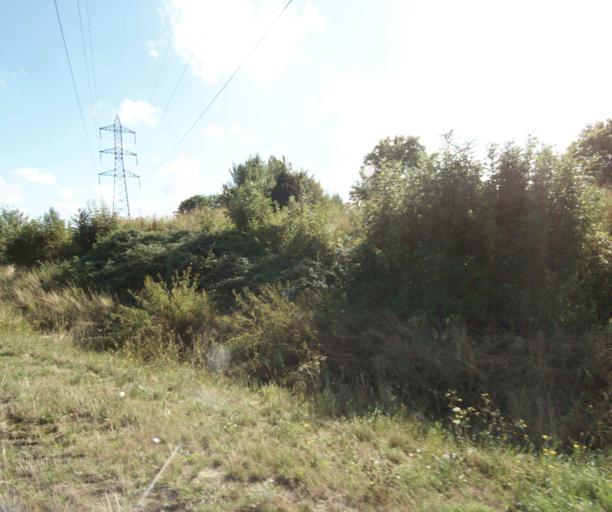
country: FR
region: Nord-Pas-de-Calais
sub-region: Departement du Nord
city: Sailly-lez-Lannoy
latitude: 50.6529
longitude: 3.2079
